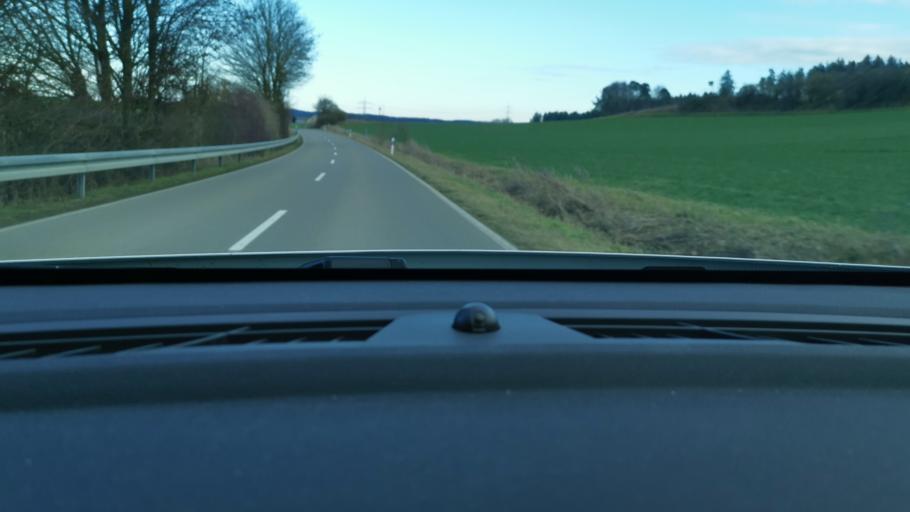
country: DE
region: Bavaria
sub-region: Swabia
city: Rehling
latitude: 48.4894
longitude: 10.9556
